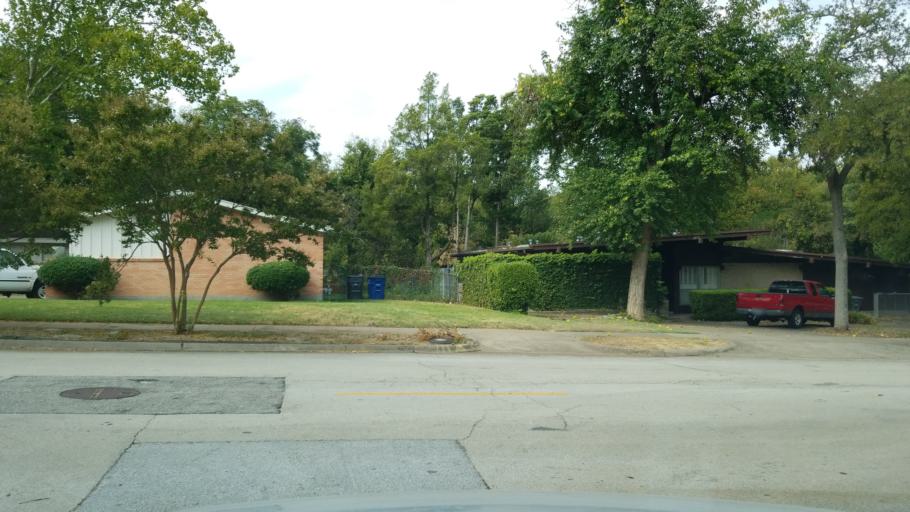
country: US
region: Texas
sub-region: Dallas County
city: Garland
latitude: 32.8716
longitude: -96.6938
